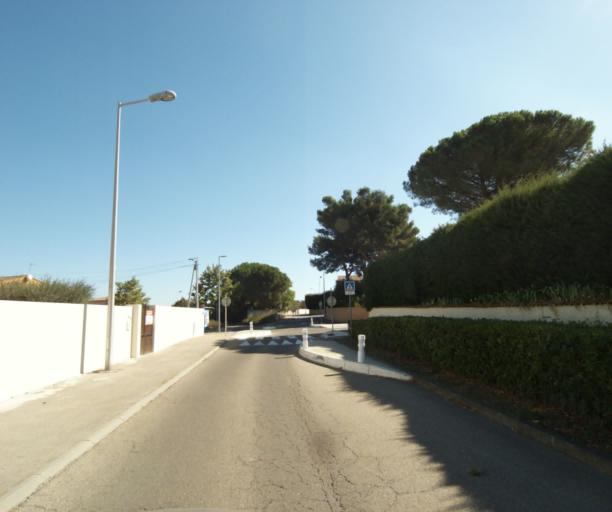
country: FR
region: Languedoc-Roussillon
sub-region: Departement du Gard
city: Bouillargues
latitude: 43.8029
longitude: 4.4290
